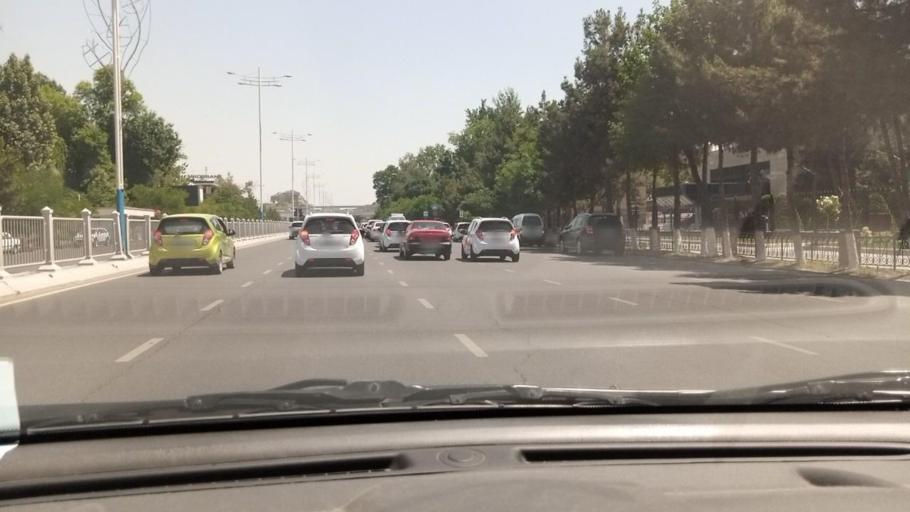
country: UZ
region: Toshkent Shahri
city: Tashkent
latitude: 41.2944
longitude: 69.2195
